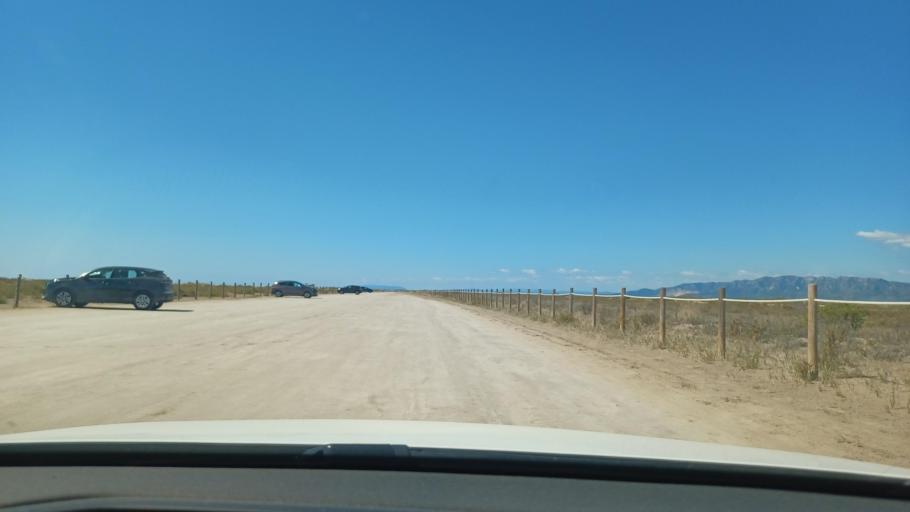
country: ES
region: Catalonia
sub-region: Provincia de Tarragona
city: Deltebre
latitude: 40.6443
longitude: 0.7596
